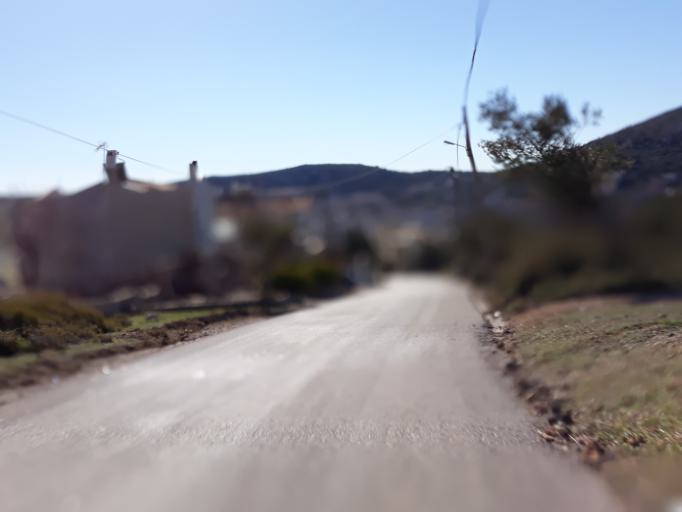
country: GR
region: Attica
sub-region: Nomarchia Dytikis Attikis
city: Fyli
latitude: 38.1124
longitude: 23.6742
